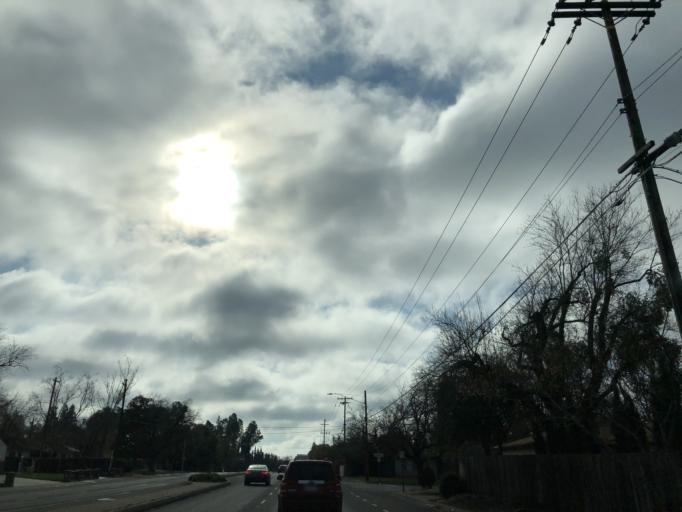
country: US
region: California
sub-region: Sacramento County
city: Arden-Arcade
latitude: 38.5835
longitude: -121.3831
